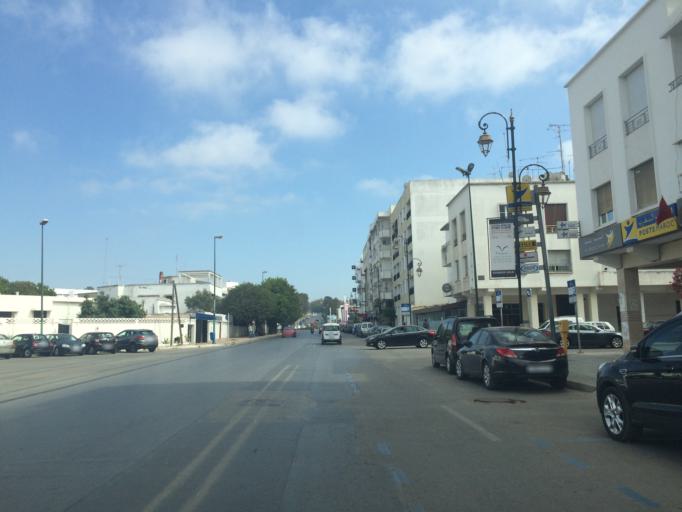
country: MA
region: Rabat-Sale-Zemmour-Zaer
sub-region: Rabat
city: Rabat
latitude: 34.0009
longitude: -6.8451
